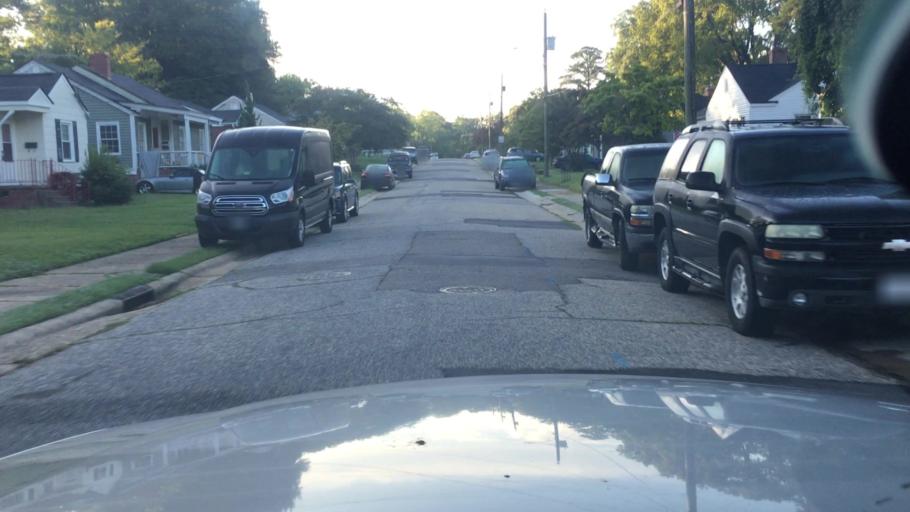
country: US
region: North Carolina
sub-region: Cumberland County
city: Fayetteville
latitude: 35.0612
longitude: -78.9046
